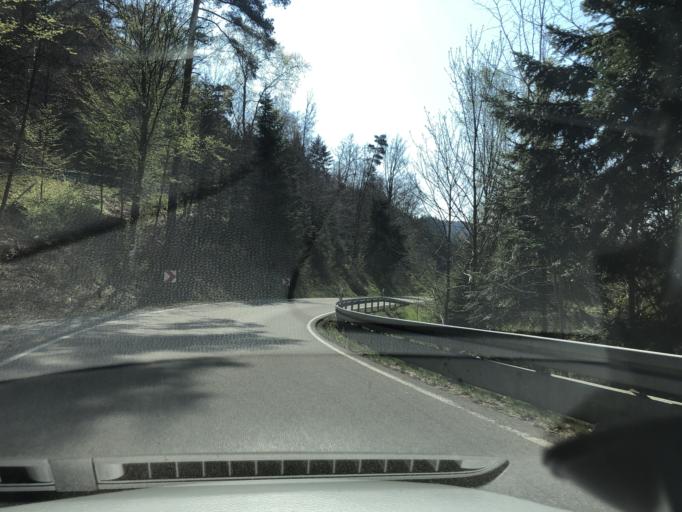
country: DE
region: Baden-Wuerttemberg
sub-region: Karlsruhe Region
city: Unterreichenbach
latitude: 48.8242
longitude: 8.7146
